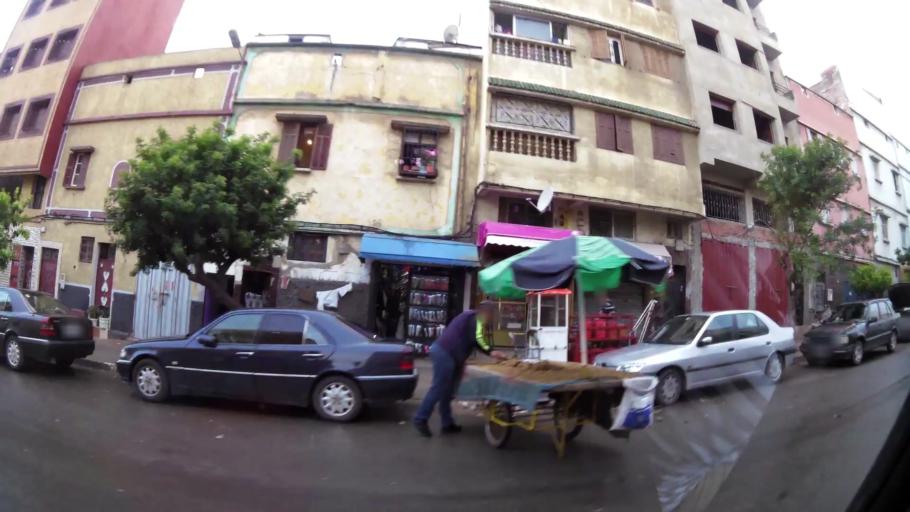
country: MA
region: Grand Casablanca
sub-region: Casablanca
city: Casablanca
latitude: 33.5500
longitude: -7.5760
